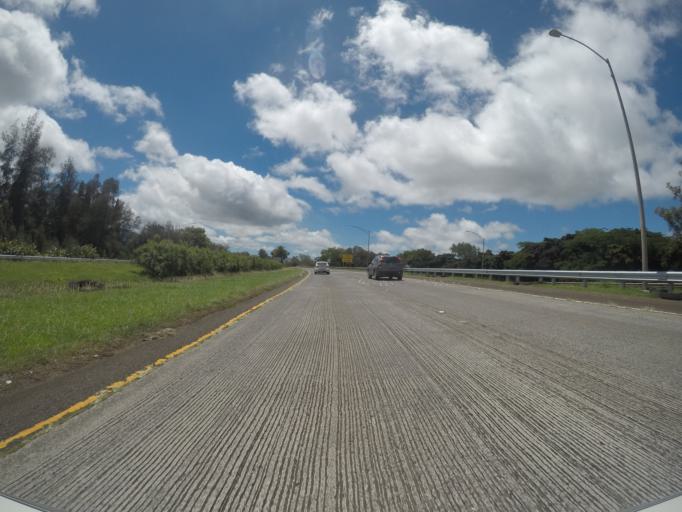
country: US
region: Hawaii
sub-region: Honolulu County
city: Wahiawa
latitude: 21.4887
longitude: -158.0268
